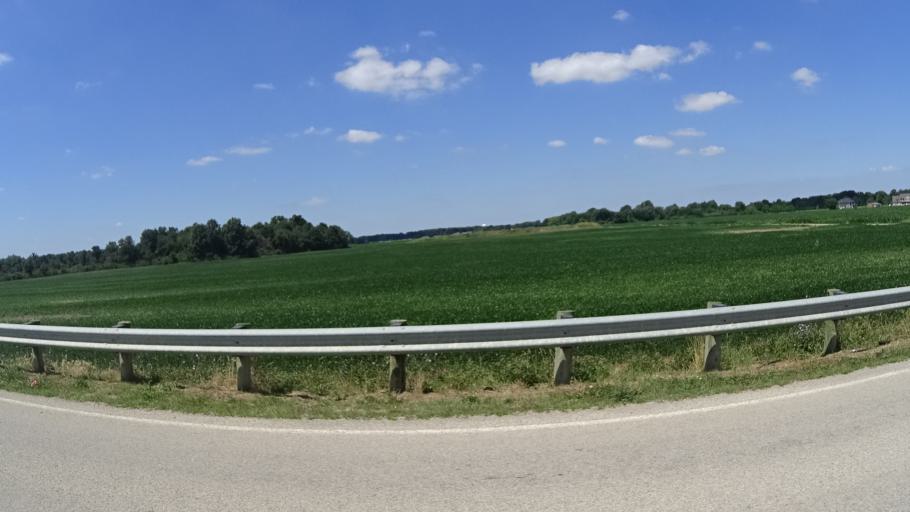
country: US
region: Ohio
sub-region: Erie County
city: Huron
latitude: 41.4070
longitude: -82.6158
